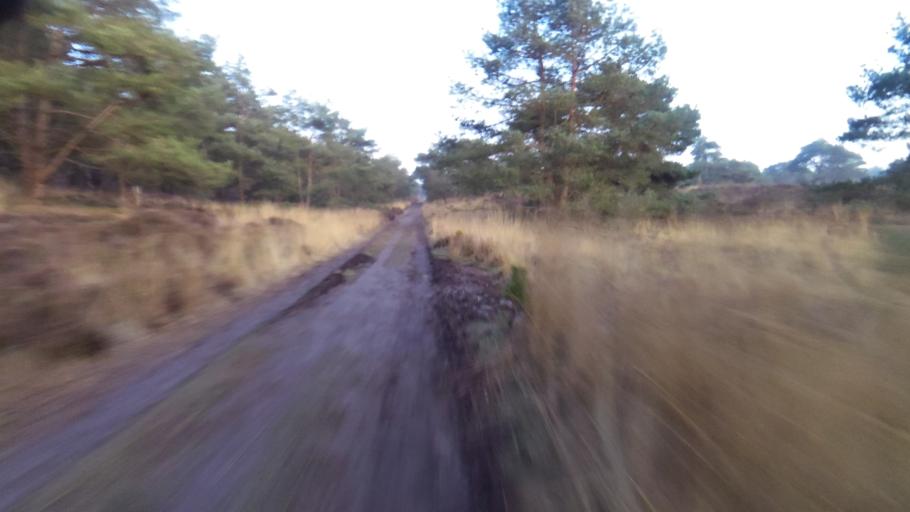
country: NL
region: Gelderland
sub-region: Gemeente Apeldoorn
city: Uddel
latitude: 52.2547
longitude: 5.8196
